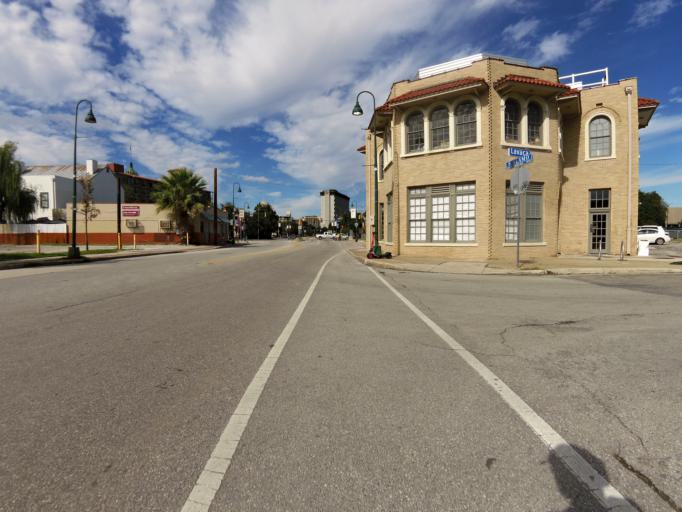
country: US
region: Texas
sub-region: Bexar County
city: San Antonio
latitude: 29.4175
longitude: -98.4882
